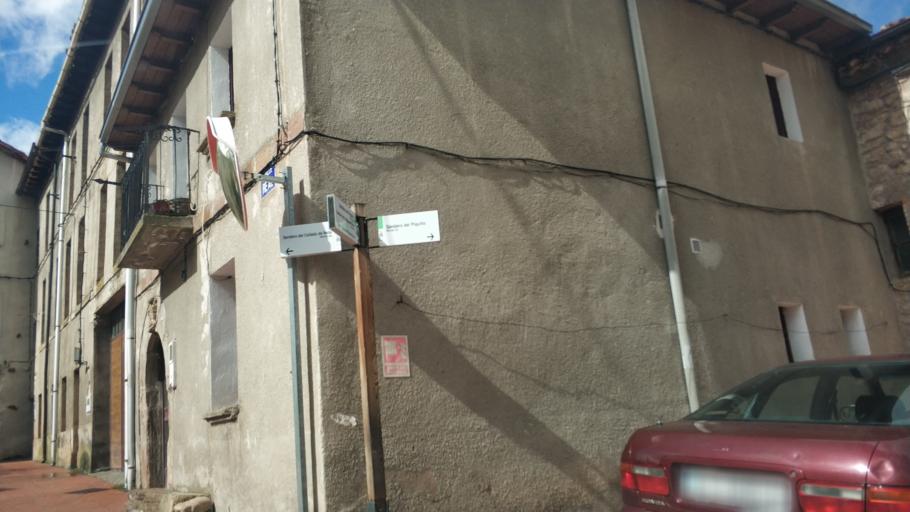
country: ES
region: Castille and Leon
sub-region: Provincia de Burgos
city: Neila
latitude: 42.0603
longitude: -2.9965
